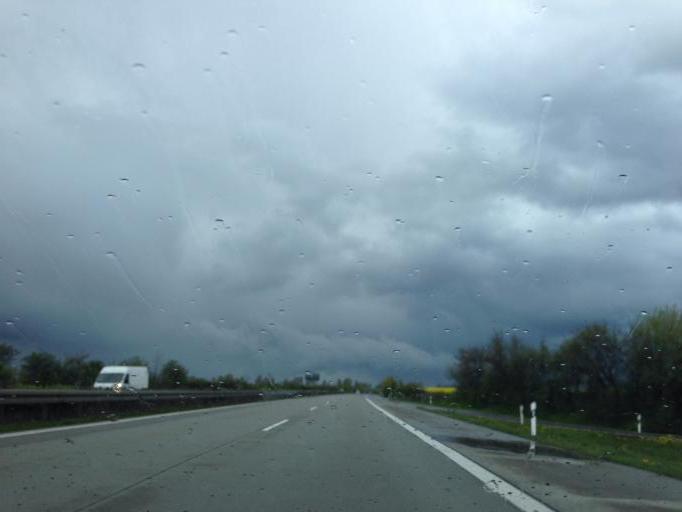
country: DE
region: Saxony-Anhalt
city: Hohendodeleben
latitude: 52.0846
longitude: 11.5390
